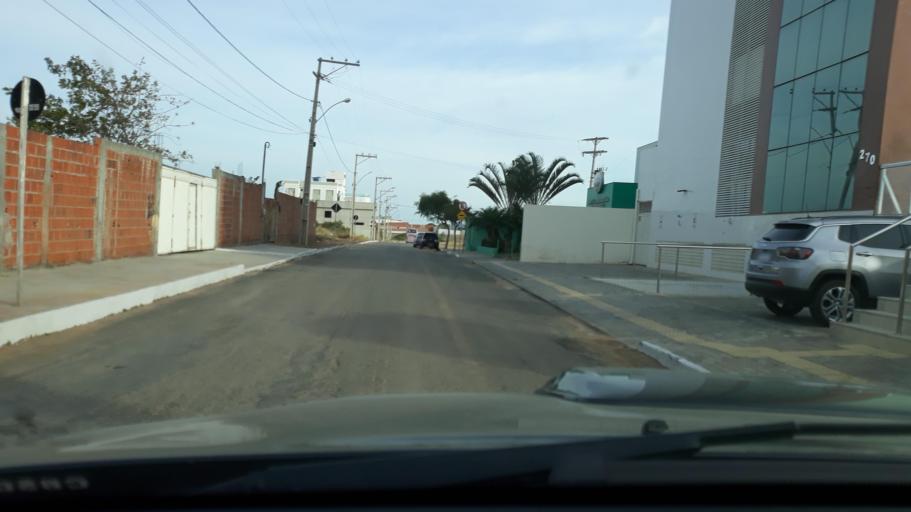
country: BR
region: Bahia
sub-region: Guanambi
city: Guanambi
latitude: -14.2118
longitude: -42.7665
